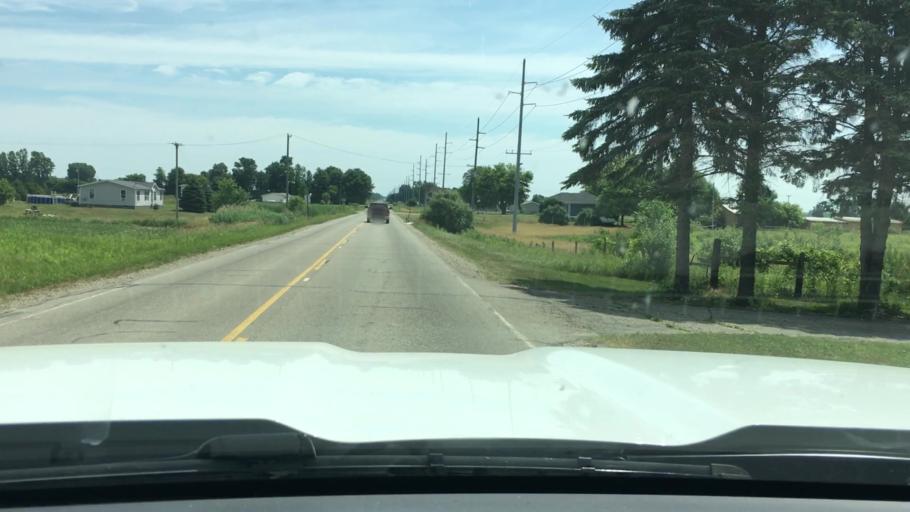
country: US
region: Michigan
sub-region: Sanilac County
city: Brown City
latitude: 43.2561
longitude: -83.0024
